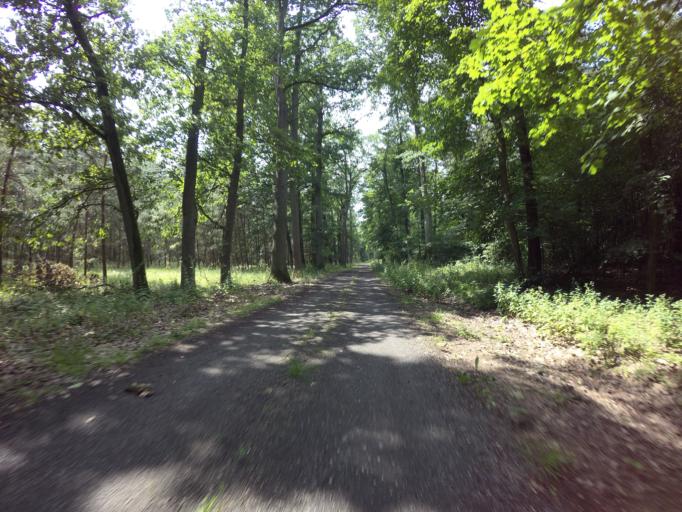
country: PL
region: Kujawsko-Pomorskie
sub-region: Powiat bydgoski
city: Koronowo
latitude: 53.3646
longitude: 17.9853
